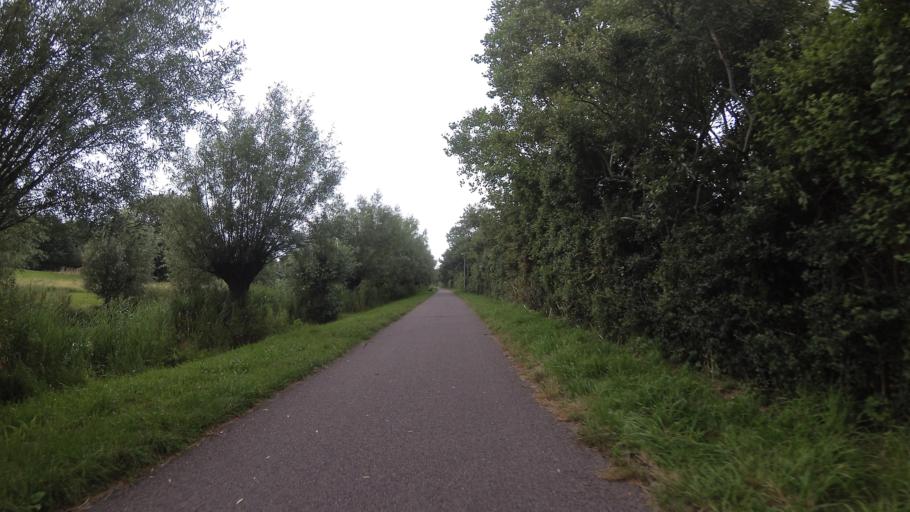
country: NL
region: North Holland
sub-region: Gemeente Den Helder
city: Den Helder
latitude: 52.8946
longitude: 4.7353
